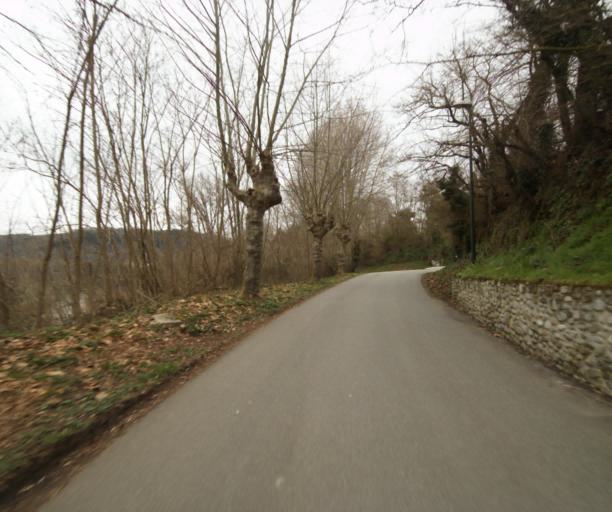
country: FR
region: Midi-Pyrenees
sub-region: Departement de l'Ariege
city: Pamiers
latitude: 43.1657
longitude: 1.5973
